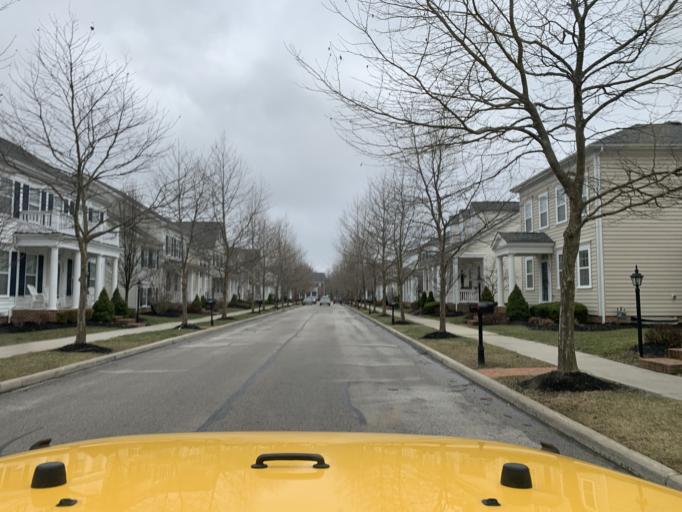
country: US
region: Ohio
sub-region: Franklin County
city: New Albany
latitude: 40.0885
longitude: -82.8063
